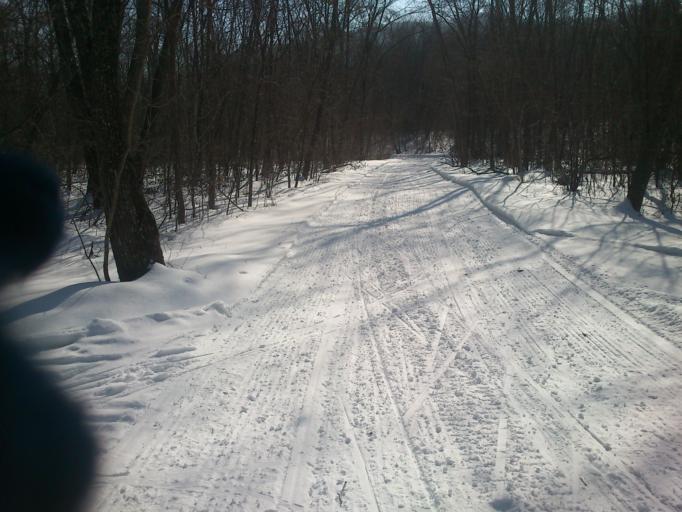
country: RU
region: Primorskiy
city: Volchanets
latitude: 43.1699
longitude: 132.7322
